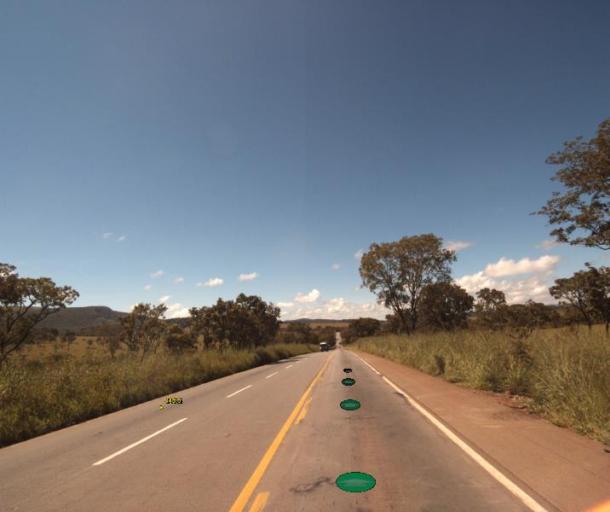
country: BR
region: Goias
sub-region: Jaragua
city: Jaragua
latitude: -15.6272
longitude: -49.3846
